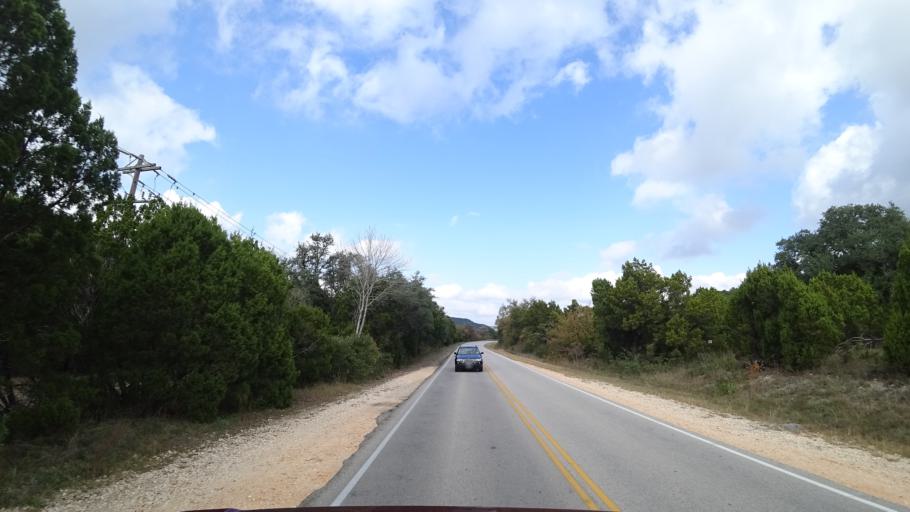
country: US
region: Texas
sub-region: Travis County
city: Hudson Bend
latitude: 30.4153
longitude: -97.8679
